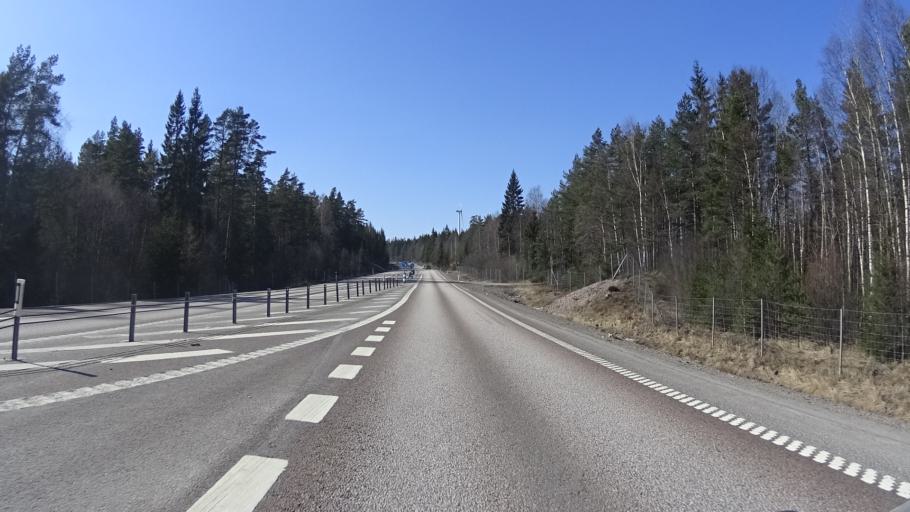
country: SE
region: Vaermland
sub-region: Kristinehamns Kommun
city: Bjorneborg
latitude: 59.3108
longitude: 14.2745
